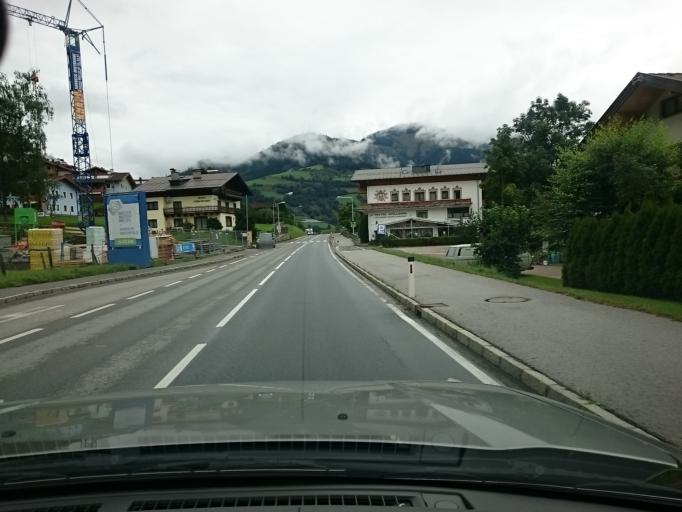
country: AT
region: Salzburg
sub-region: Politischer Bezirk Zell am See
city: Bruck an der Grossglocknerstrasse
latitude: 47.2710
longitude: 12.8252
